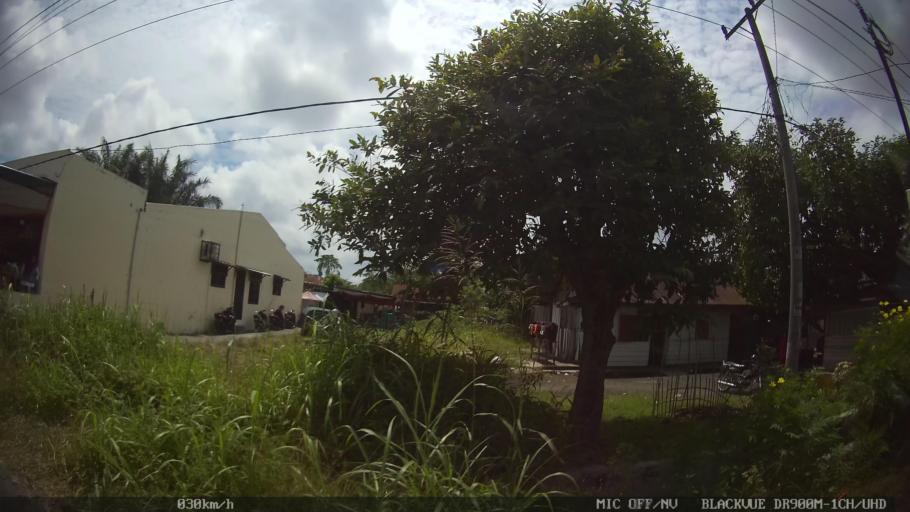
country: ID
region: North Sumatra
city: Percut
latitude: 3.6170
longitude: 98.7638
